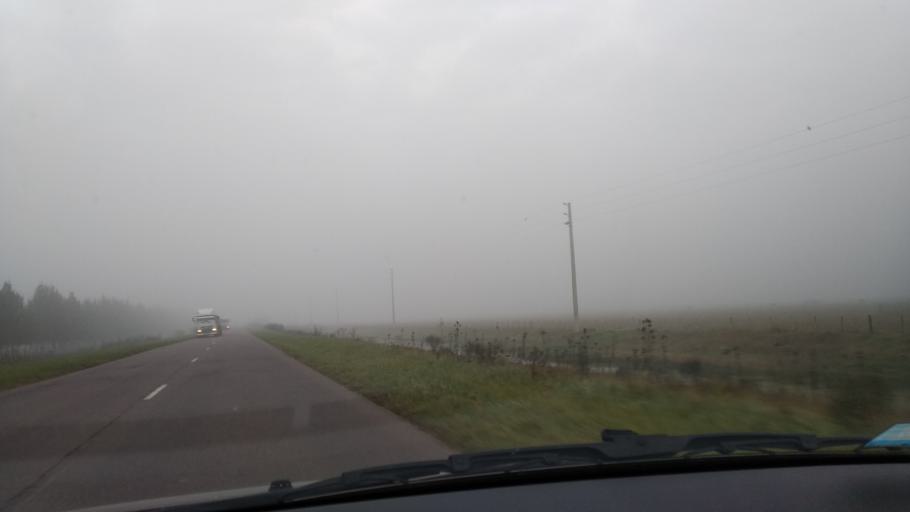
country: AR
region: Buenos Aires
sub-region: Partido de San Vicente
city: San Vicente
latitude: -35.2474
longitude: -58.4887
